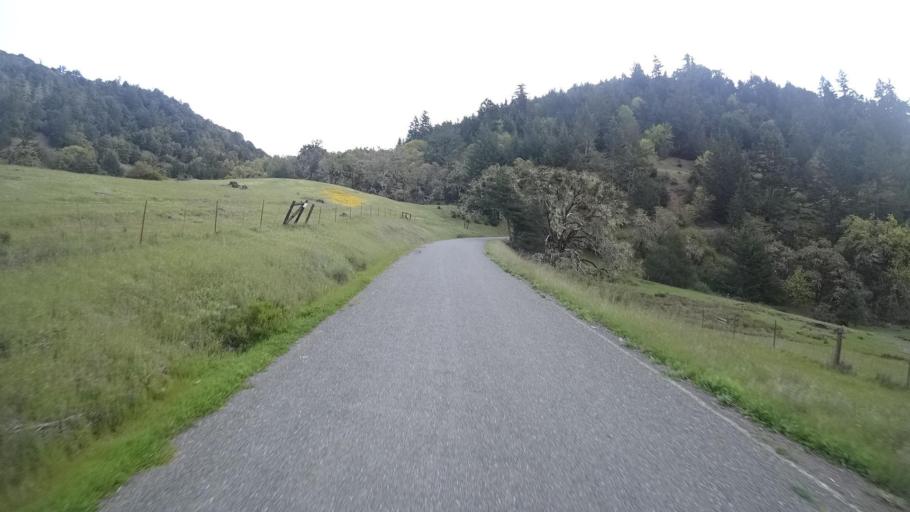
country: US
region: California
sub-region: Humboldt County
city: Redway
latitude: 40.1588
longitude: -123.5576
